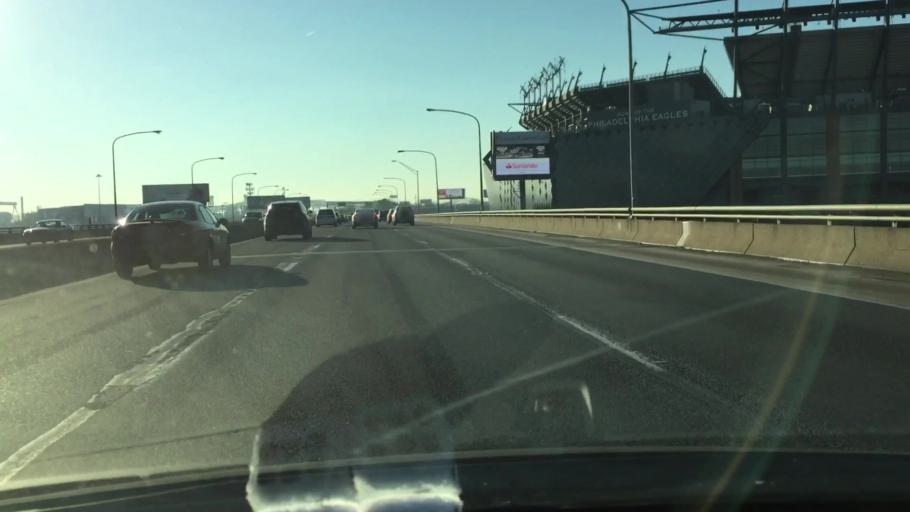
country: US
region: New Jersey
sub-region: Gloucester County
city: National Park
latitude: 39.8999
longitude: -75.1640
